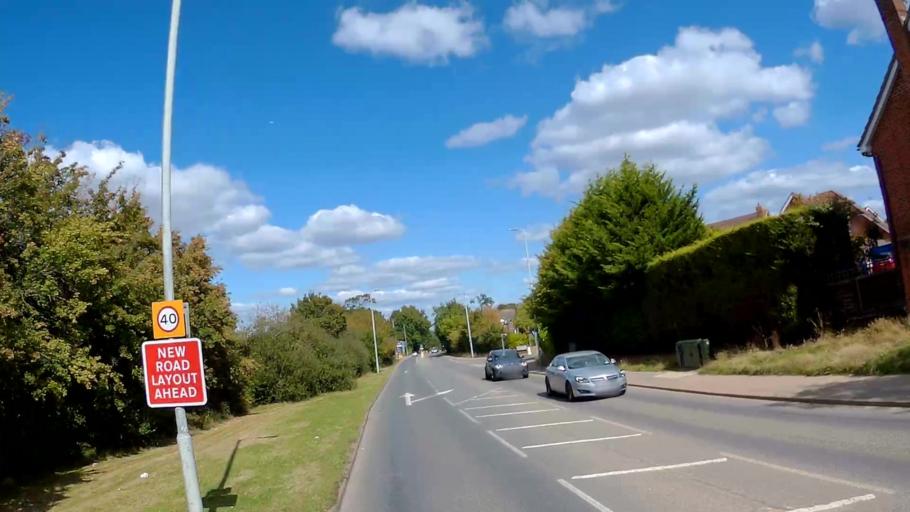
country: GB
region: England
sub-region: Bracknell Forest
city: Binfield
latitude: 51.4235
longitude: -0.7775
